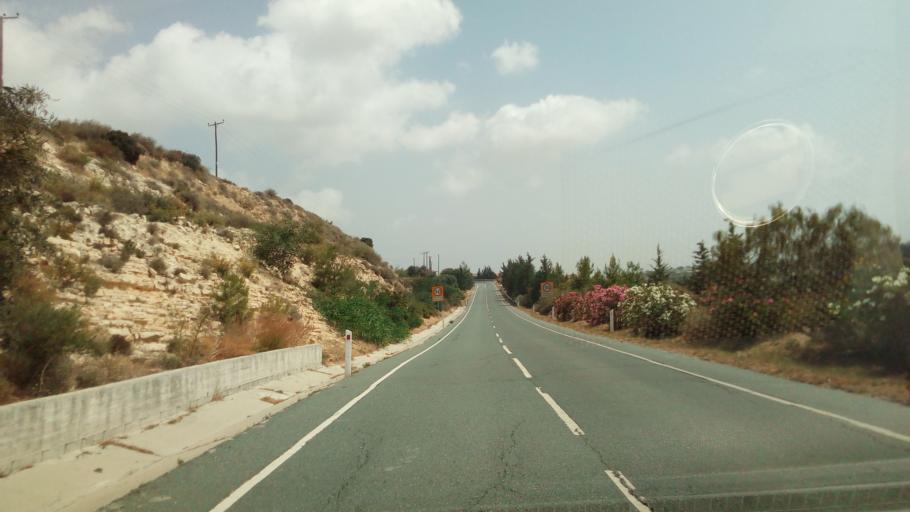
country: CY
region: Larnaka
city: Kofinou
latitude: 34.8070
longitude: 33.3258
